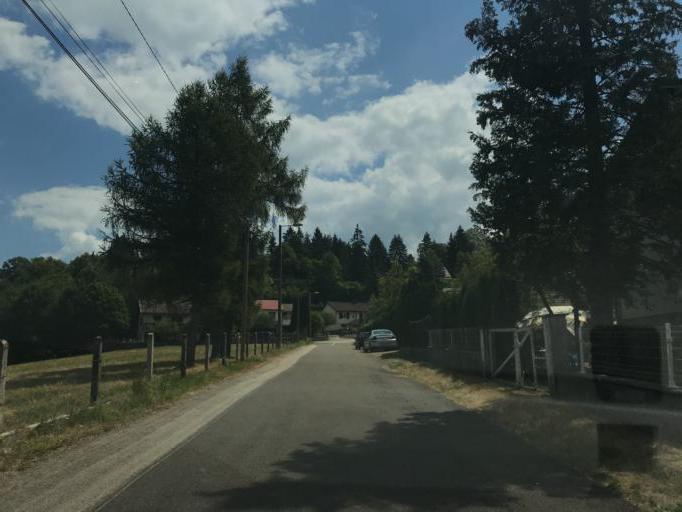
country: FR
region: Franche-Comte
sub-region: Departement du Jura
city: Clairvaux-les-Lacs
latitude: 46.5725
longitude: 5.7562
